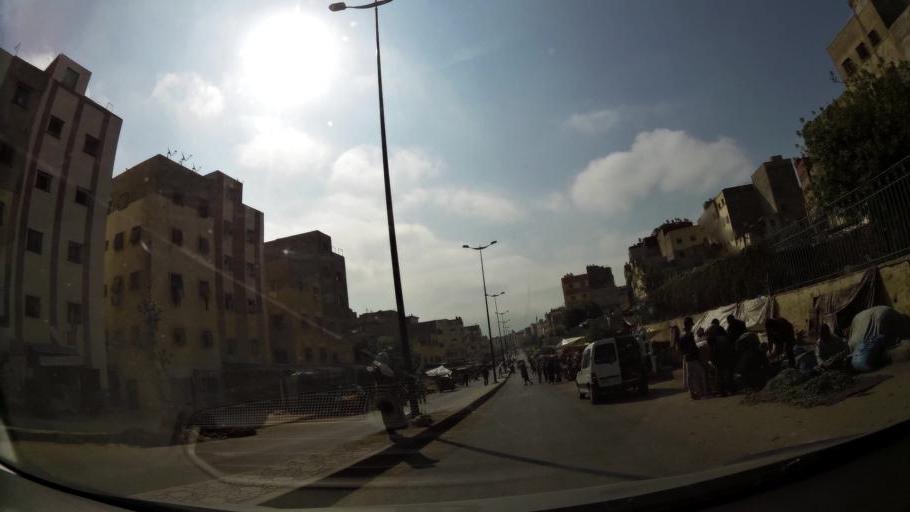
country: MA
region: Fes-Boulemane
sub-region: Fes
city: Fes
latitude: 34.0698
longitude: -5.0105
